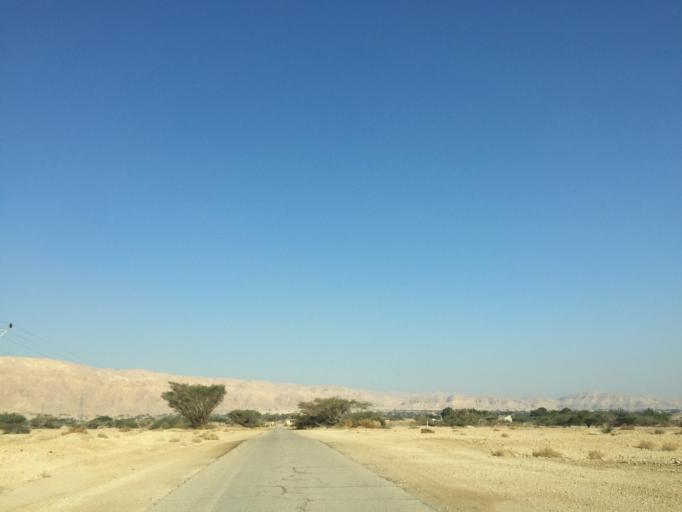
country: JO
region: Ma'an
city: Al Quwayrah
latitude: 29.8429
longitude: 35.0295
